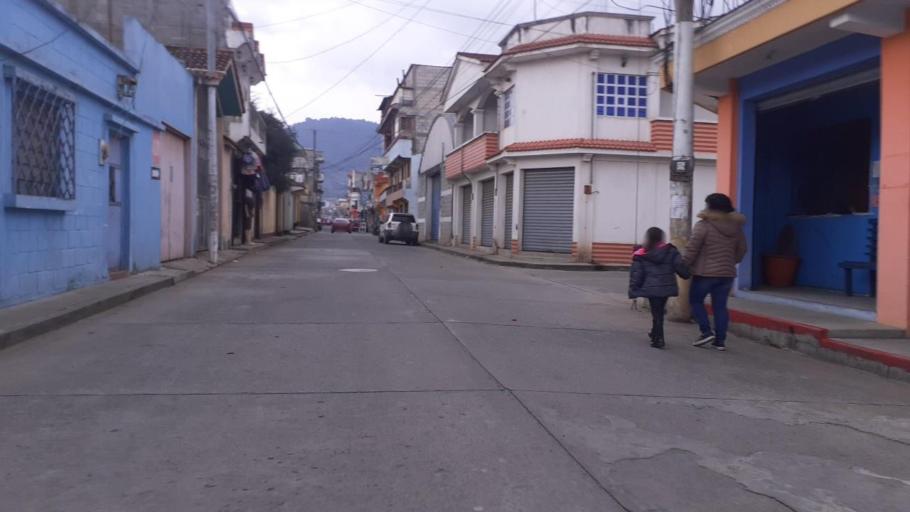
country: GT
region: Quetzaltenango
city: Ostuncalco
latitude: 14.8703
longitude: -91.6186
